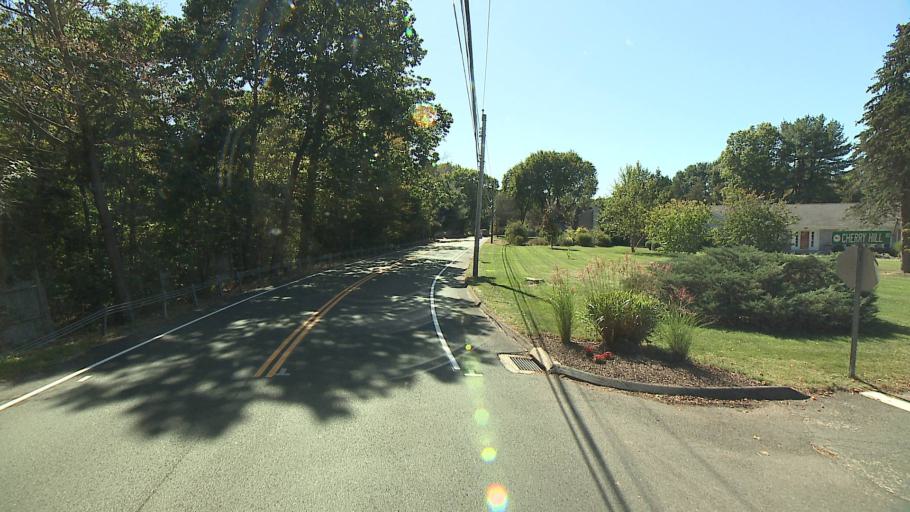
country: US
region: Connecticut
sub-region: New Haven County
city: Orange
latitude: 41.2946
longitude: -73.0258
